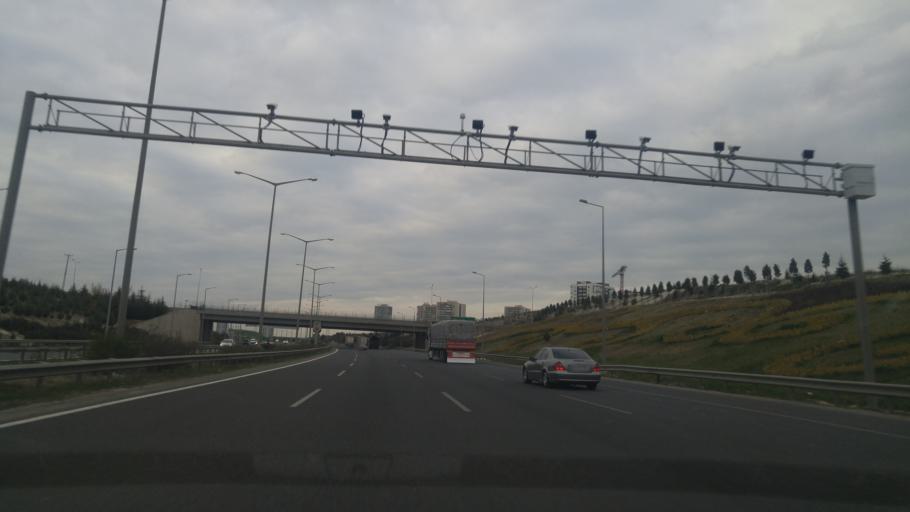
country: TR
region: Ankara
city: Etimesgut
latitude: 39.9952
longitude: 32.6373
